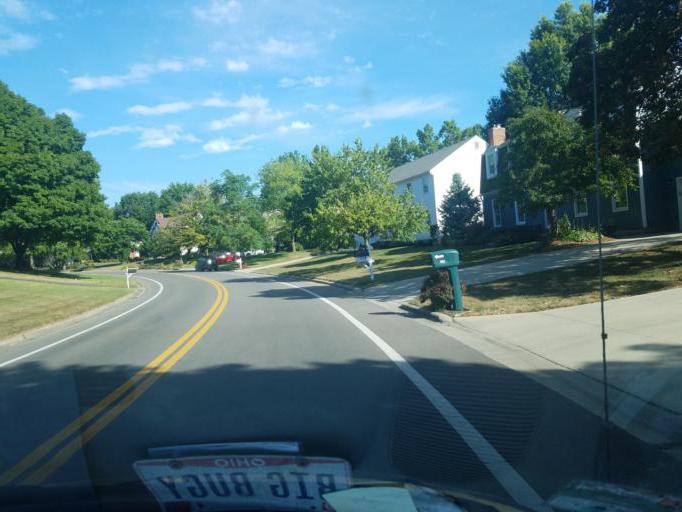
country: US
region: Ohio
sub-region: Delaware County
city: Powell
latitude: 40.1296
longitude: -83.0443
